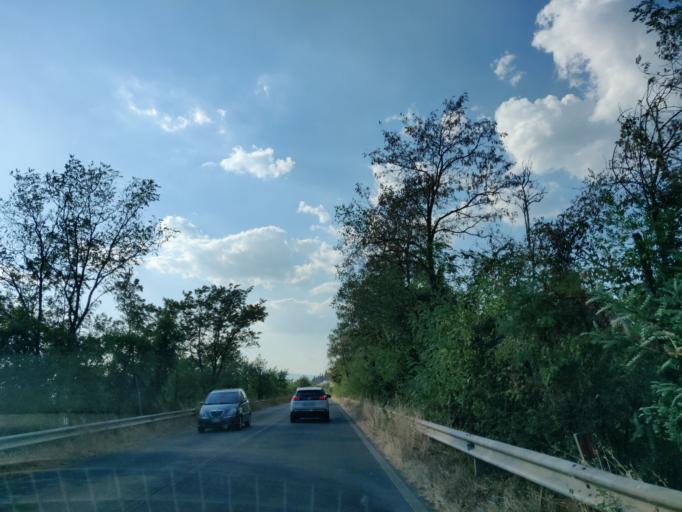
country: IT
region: Latium
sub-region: Provincia di Viterbo
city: Proceno
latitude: 42.7727
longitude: 11.8507
